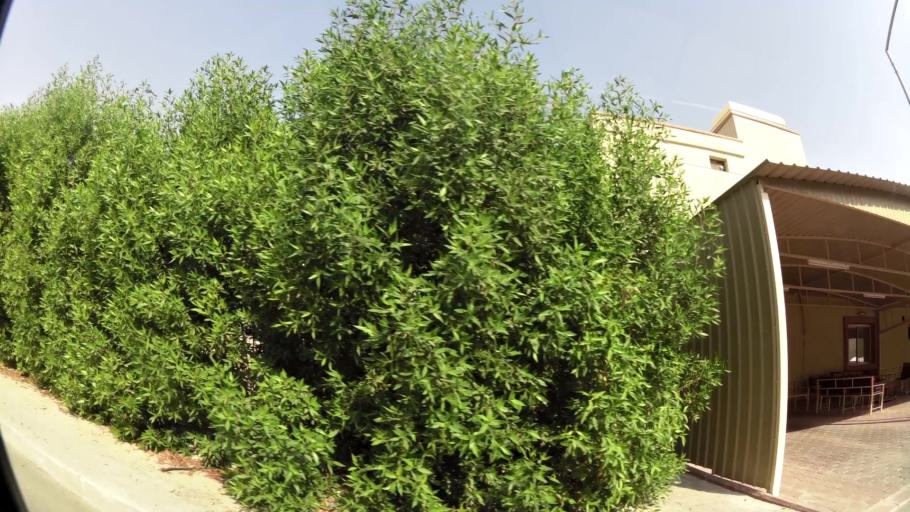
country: KW
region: Muhafazat al Jahra'
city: Al Jahra'
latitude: 29.3580
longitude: 47.7582
